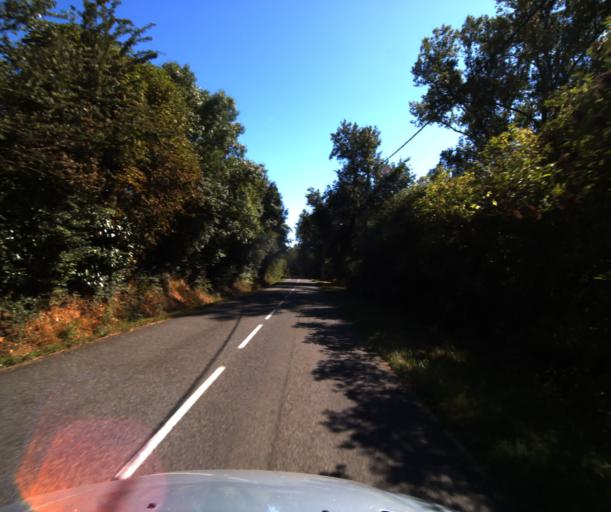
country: FR
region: Midi-Pyrenees
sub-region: Departement de la Haute-Garonne
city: Eaunes
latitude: 43.4392
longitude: 1.3275
